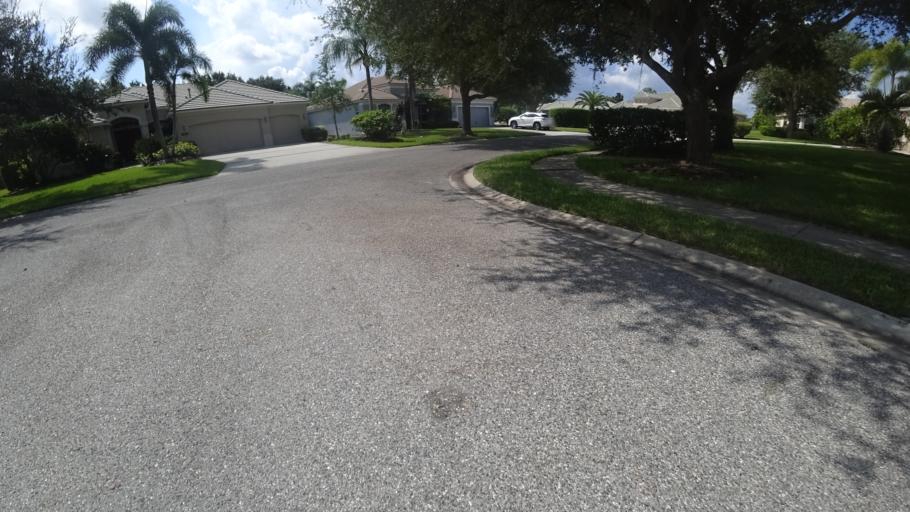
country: US
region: Florida
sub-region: Sarasota County
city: The Meadows
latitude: 27.4175
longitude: -82.4192
